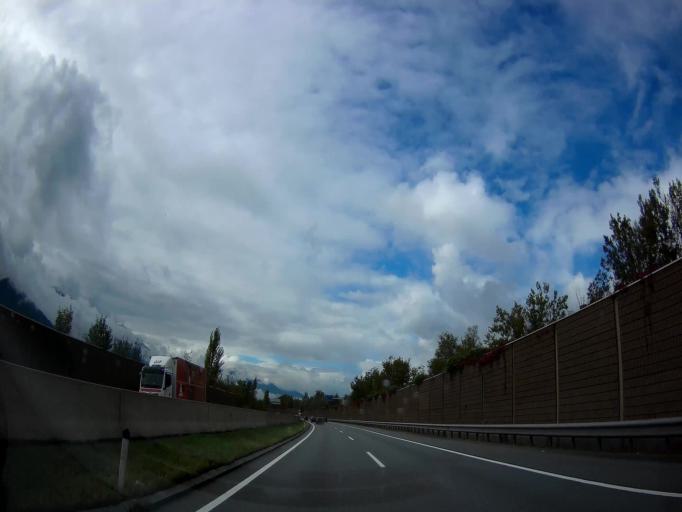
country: AT
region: Tyrol
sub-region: Politischer Bezirk Innsbruck Land
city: Baumkirchen
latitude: 47.2994
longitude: 11.5743
